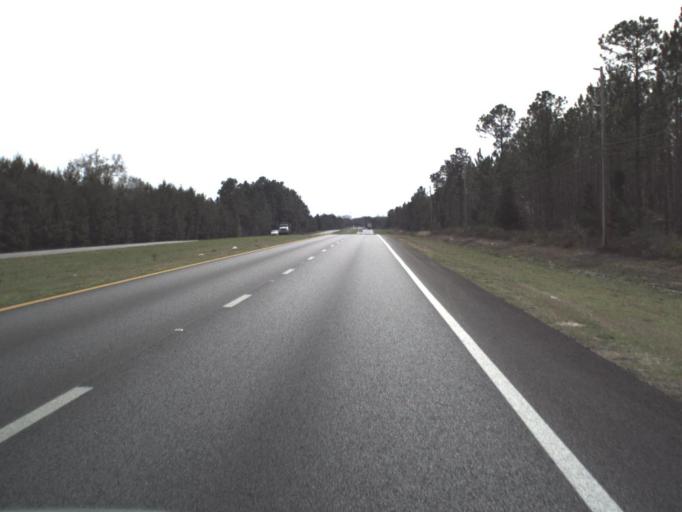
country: US
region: Florida
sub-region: Bay County
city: Youngstown
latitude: 30.3942
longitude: -85.4357
